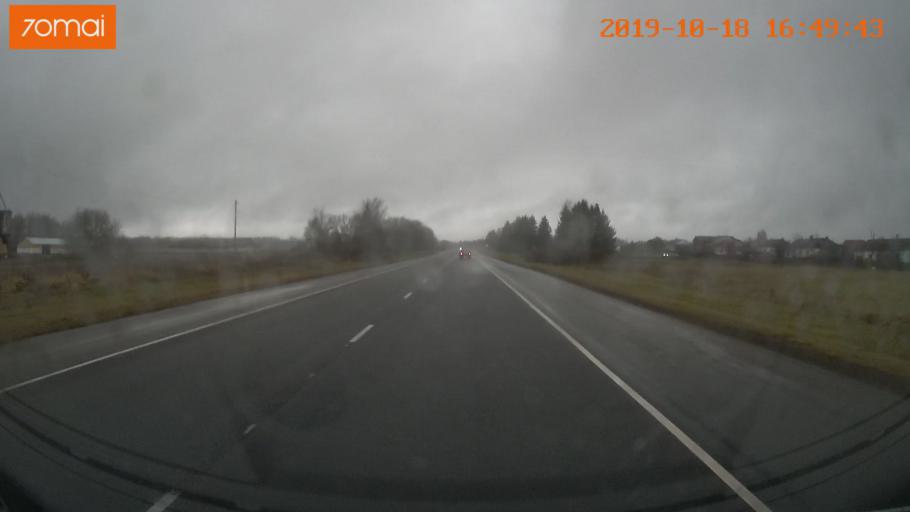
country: RU
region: Vladimir
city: Kideksha
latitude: 56.5614
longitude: 40.5493
